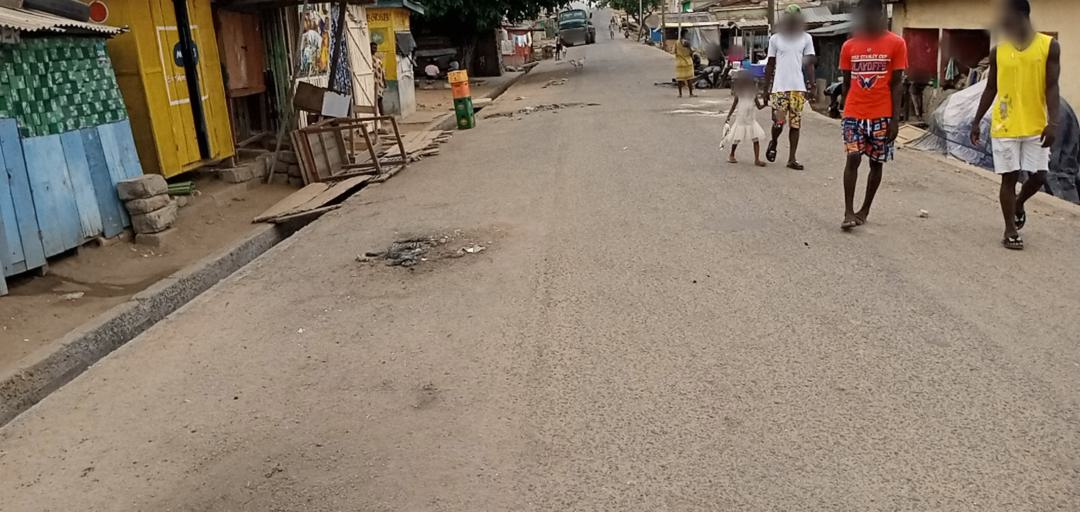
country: GH
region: Central
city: Winneba
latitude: 5.3447
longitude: -0.6219
